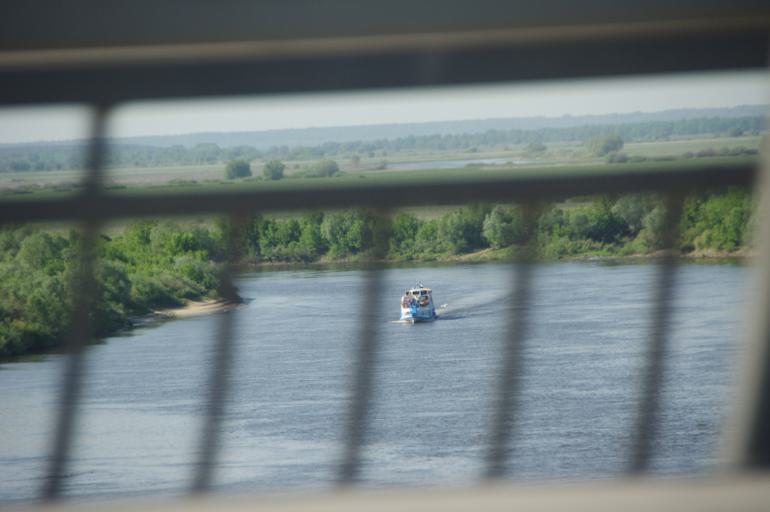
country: RU
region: Rjazan
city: Polyany
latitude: 54.6540
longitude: 39.8083
